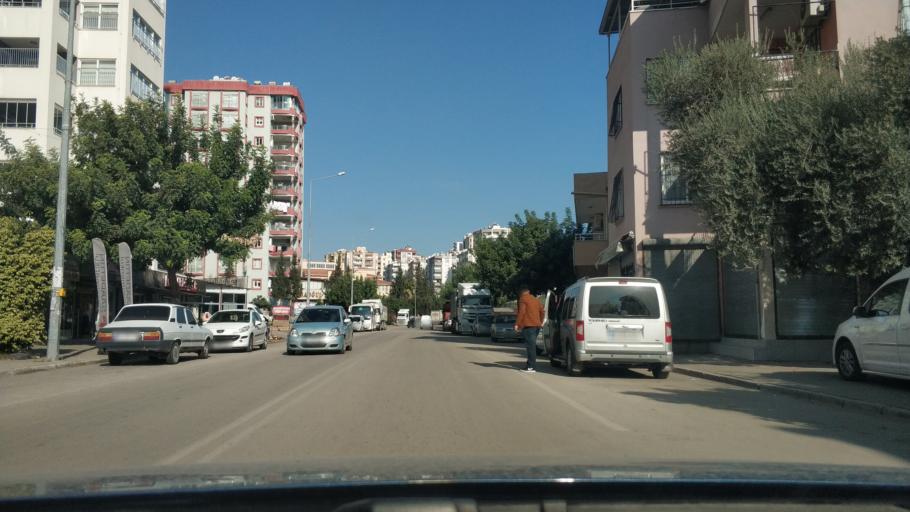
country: TR
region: Adana
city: Seyhan
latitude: 37.0205
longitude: 35.2912
